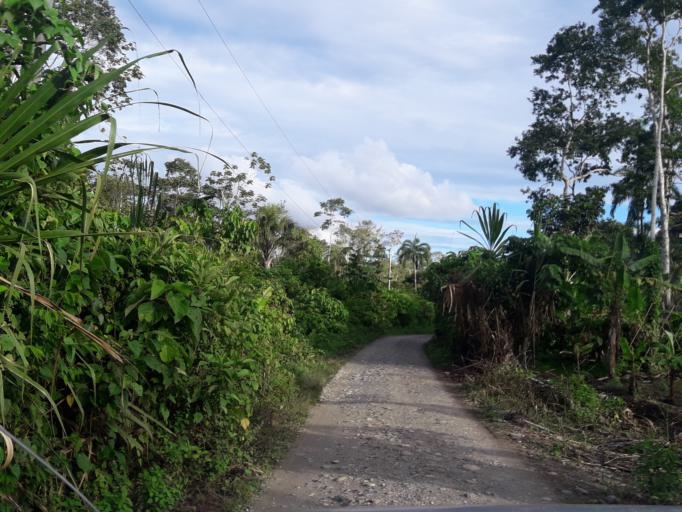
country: EC
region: Orellana
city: Boca Suno
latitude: -0.8978
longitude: -77.3092
